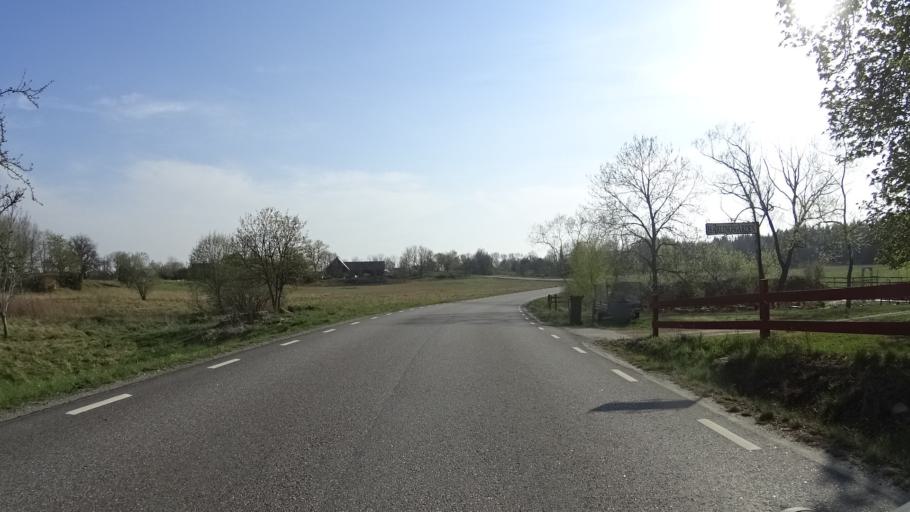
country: SE
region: Vaestra Goetaland
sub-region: Gotene Kommun
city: Goetene
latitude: 58.6239
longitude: 13.4978
